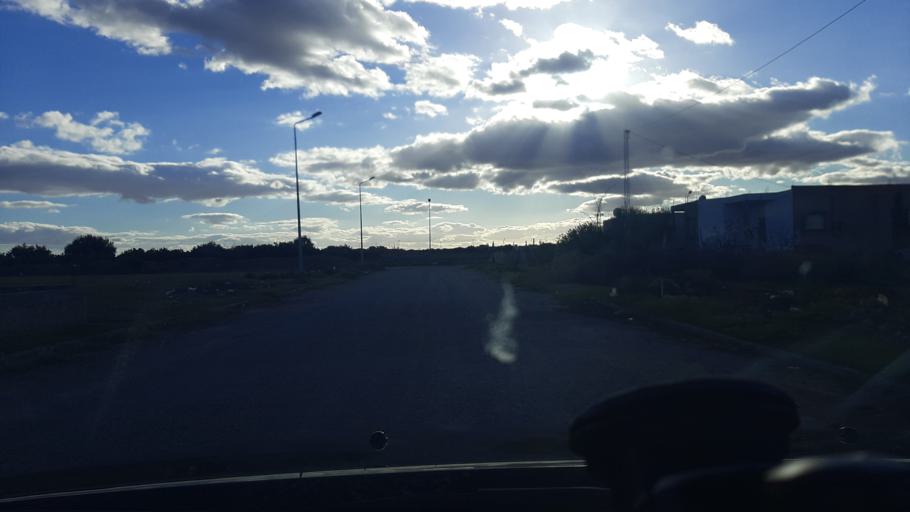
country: TN
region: Al Mahdiyah
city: Shurban
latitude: 34.9600
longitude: 10.3654
